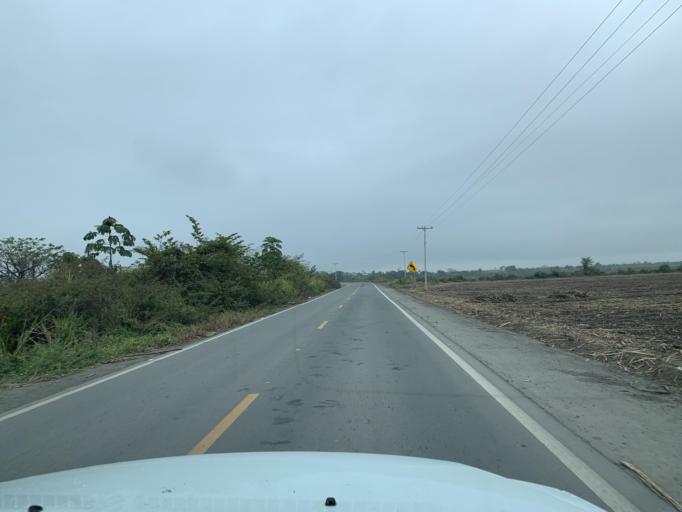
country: EC
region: Guayas
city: Coronel Marcelino Mariduena
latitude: -2.3075
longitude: -79.5075
